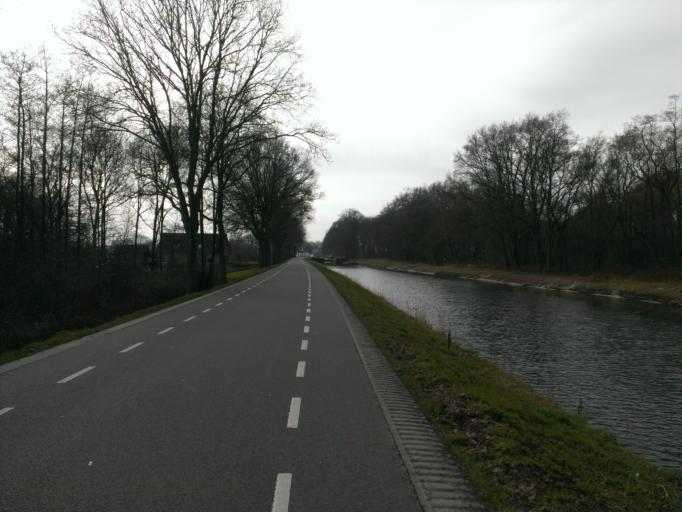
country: NL
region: Gelderland
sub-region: Gemeente Heerde
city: Heerde
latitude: 52.3842
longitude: 6.0491
